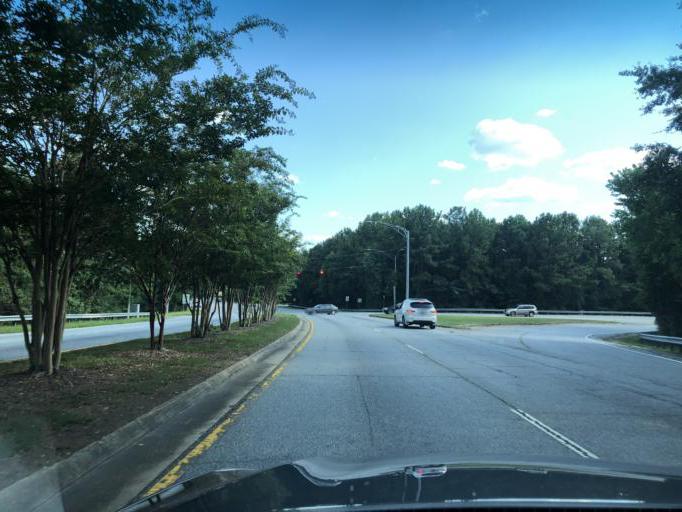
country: US
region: Georgia
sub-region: Muscogee County
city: Columbus
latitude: 32.5180
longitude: -84.9147
